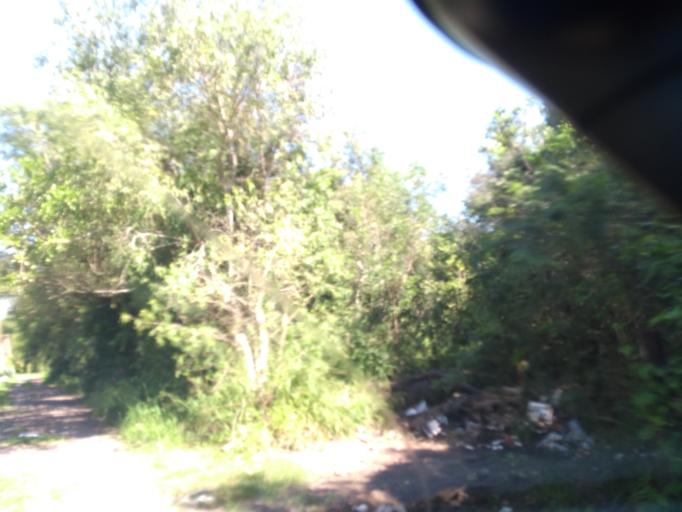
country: AR
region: Chaco
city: Resistencia
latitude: -27.4274
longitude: -58.9489
